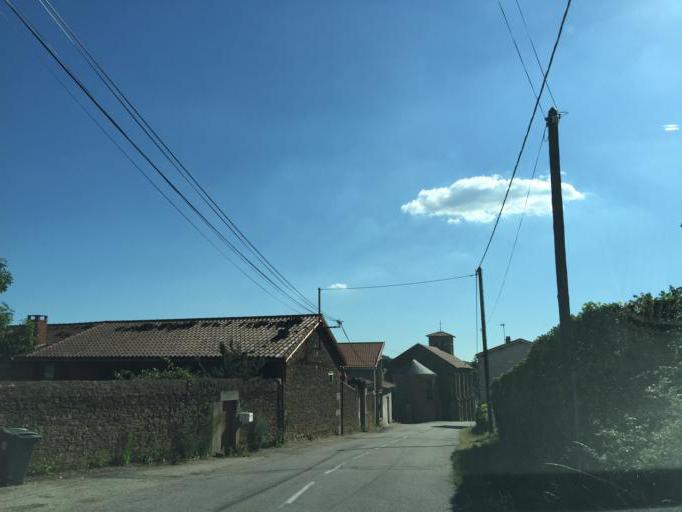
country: FR
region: Rhone-Alpes
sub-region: Departement de la Loire
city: Sorbiers
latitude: 45.4930
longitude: 4.4871
